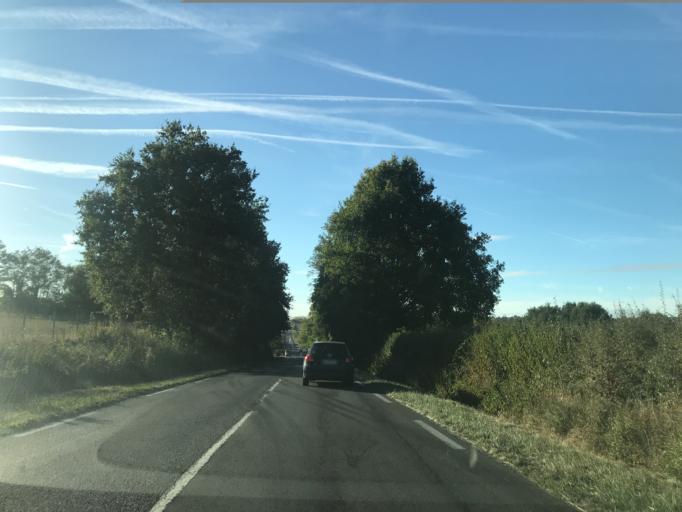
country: FR
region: Poitou-Charentes
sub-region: Departement de la Charente-Maritime
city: Montguyon
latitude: 45.2050
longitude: -0.1523
